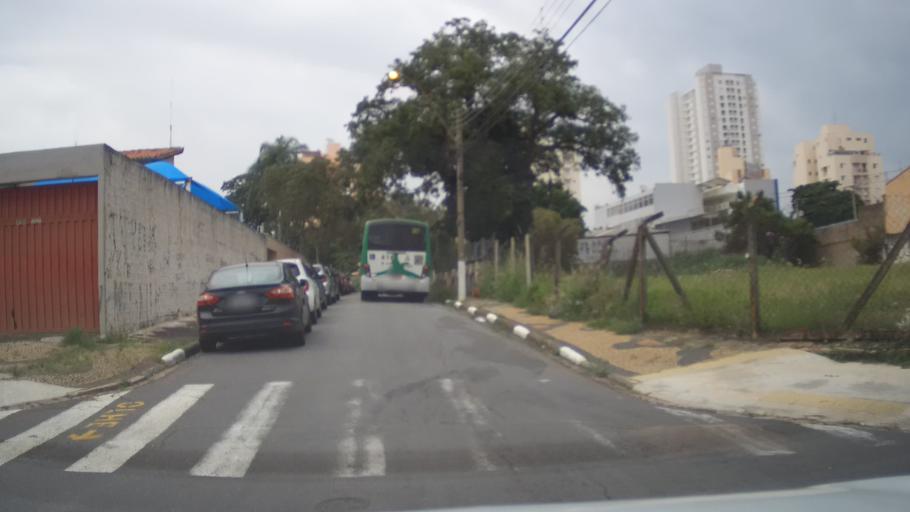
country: BR
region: Sao Paulo
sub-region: Campinas
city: Campinas
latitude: -22.9132
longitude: -47.0538
